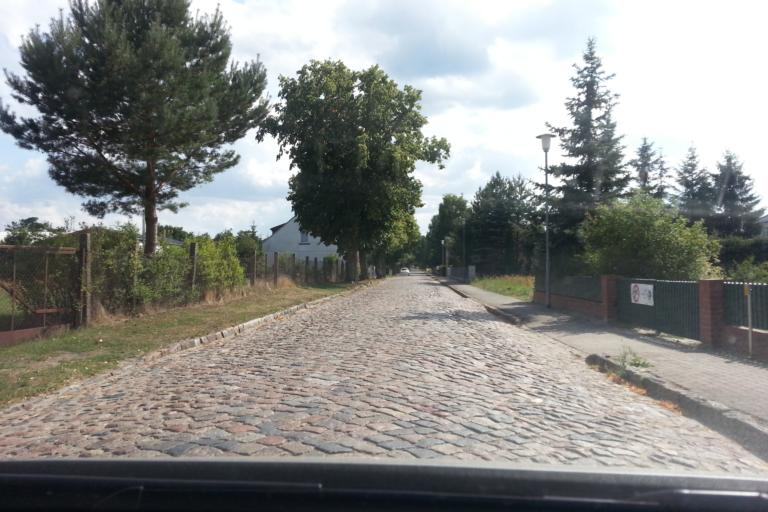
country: DE
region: Mecklenburg-Vorpommern
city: Ferdinandshof
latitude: 53.6352
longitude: 13.8691
